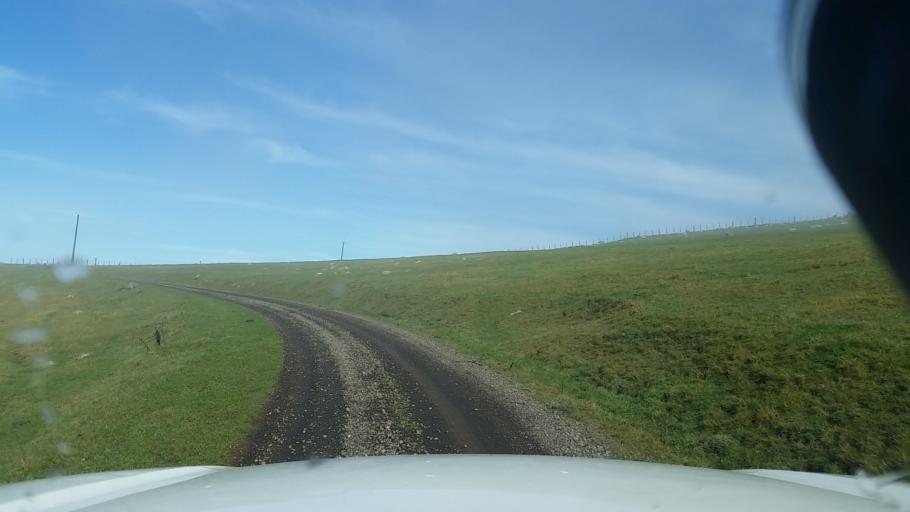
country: NZ
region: Canterbury
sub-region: Christchurch City
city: Christchurch
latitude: -43.6577
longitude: 172.8798
